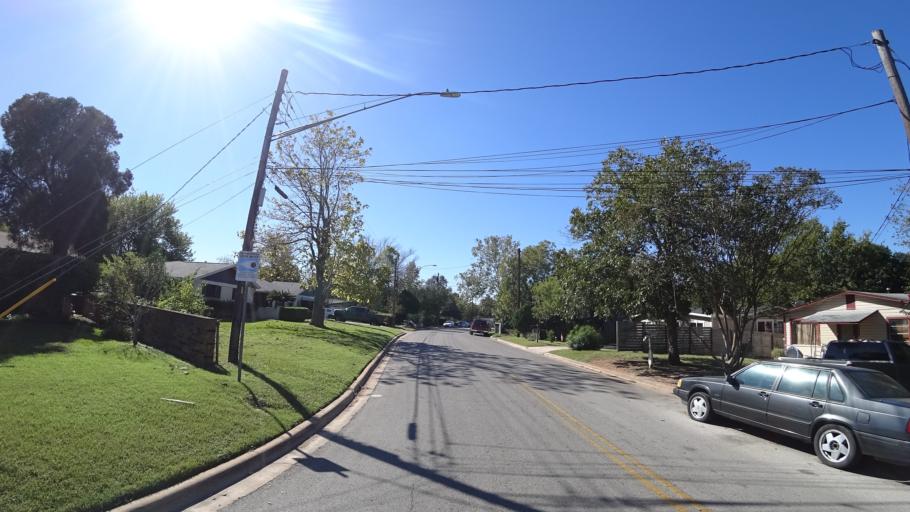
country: US
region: Texas
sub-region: Travis County
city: Austin
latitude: 30.2801
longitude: -97.6757
